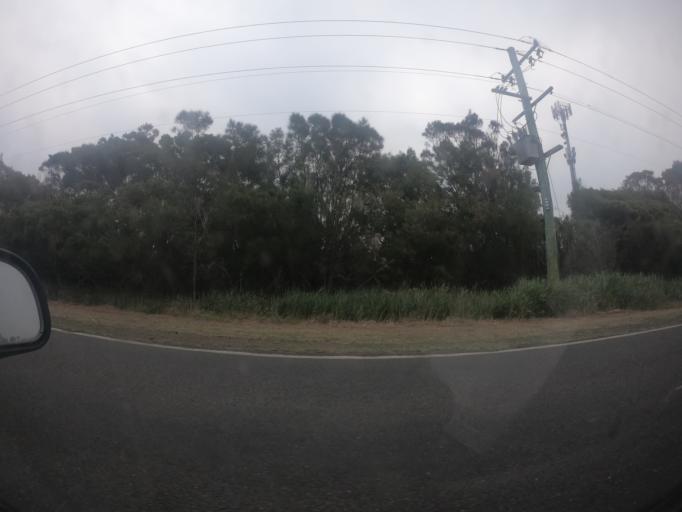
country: AU
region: New South Wales
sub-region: Shellharbour
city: Barrack Heights
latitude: -34.5690
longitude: 150.8665
